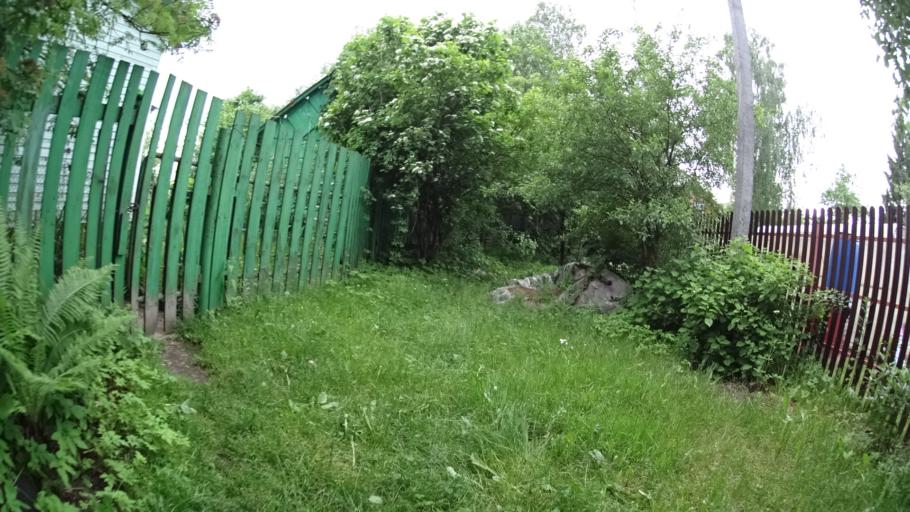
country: RU
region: Moskovskaya
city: Zelenogradskiy
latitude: 56.1241
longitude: 37.9040
